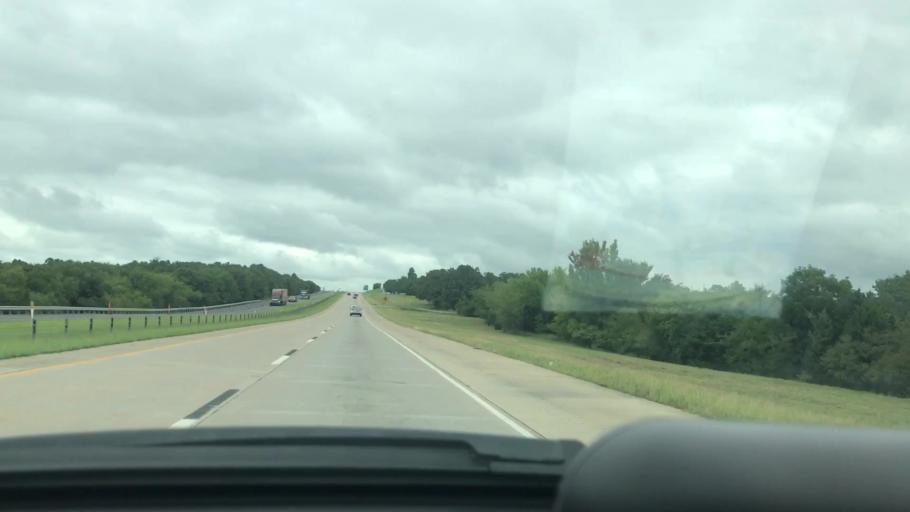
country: US
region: Oklahoma
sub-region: Pittsburg County
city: Krebs
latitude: 34.9801
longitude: -95.7227
